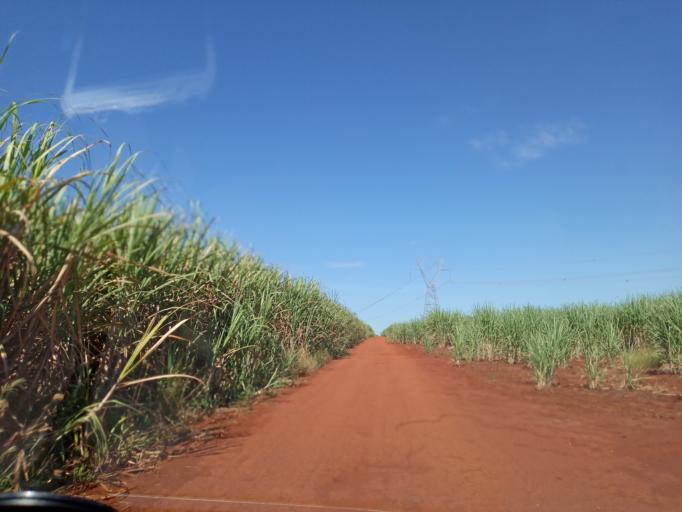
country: BR
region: Goias
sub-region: Itumbiara
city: Itumbiara
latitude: -18.4526
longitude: -49.1445
